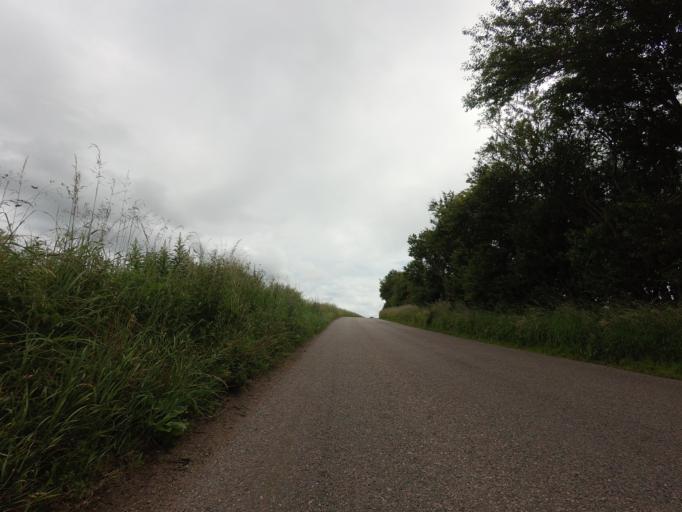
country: GB
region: Scotland
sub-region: Moray
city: Lhanbryd
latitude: 57.6596
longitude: -3.1960
